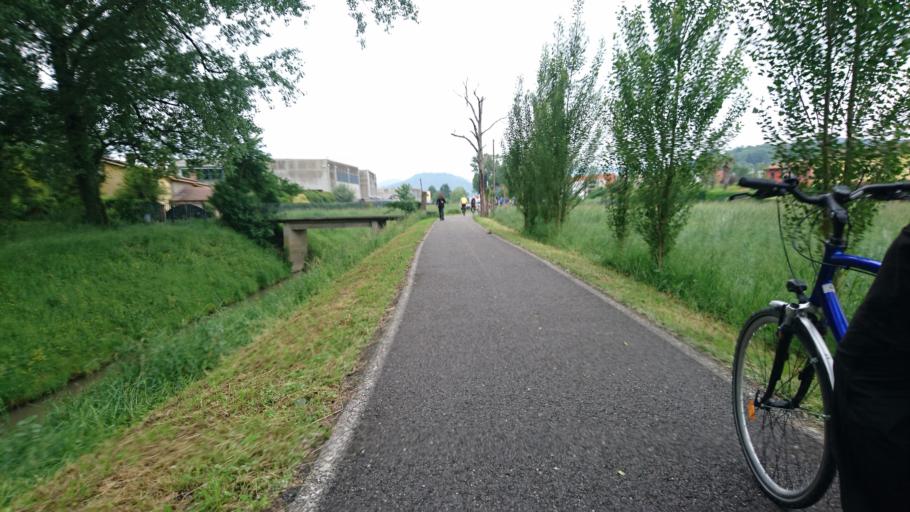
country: IT
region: Veneto
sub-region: Provincia di Padova
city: Montegrotto Terme
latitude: 45.3380
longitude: 11.7691
